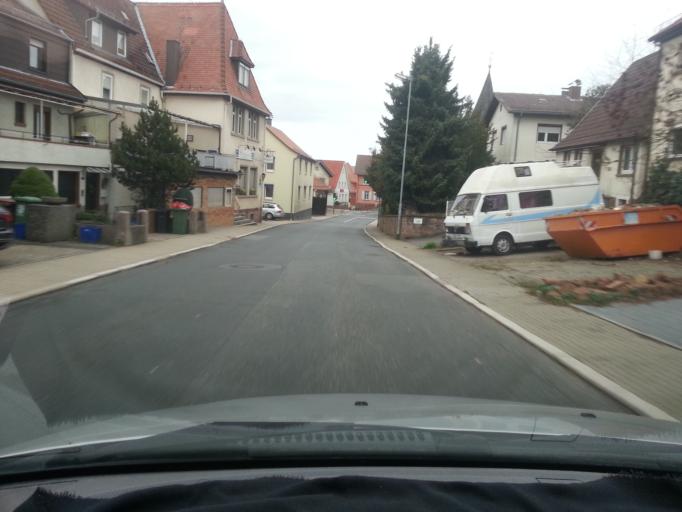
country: DE
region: Baden-Wuerttemberg
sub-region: Karlsruhe Region
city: Gaiberg
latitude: 49.3653
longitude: 8.7494
